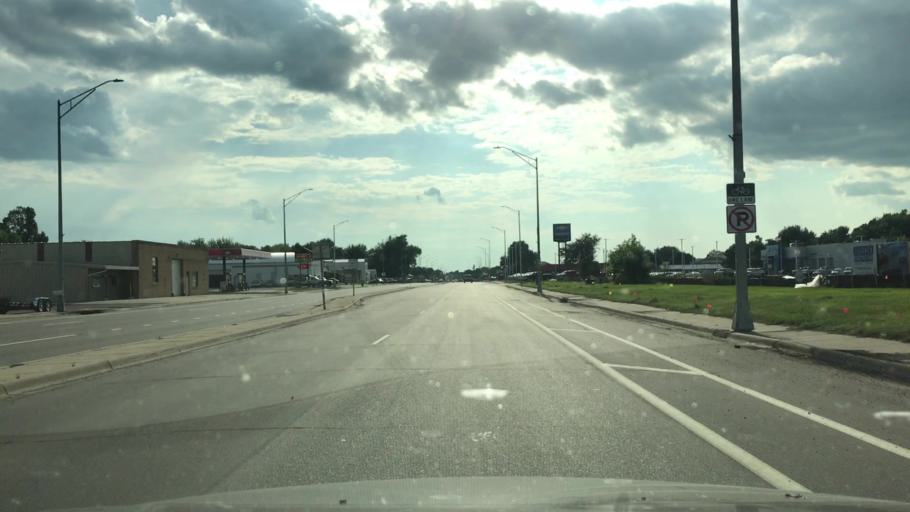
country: US
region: Minnesota
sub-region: Nobles County
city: Worthington
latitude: 43.6311
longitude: -95.5843
